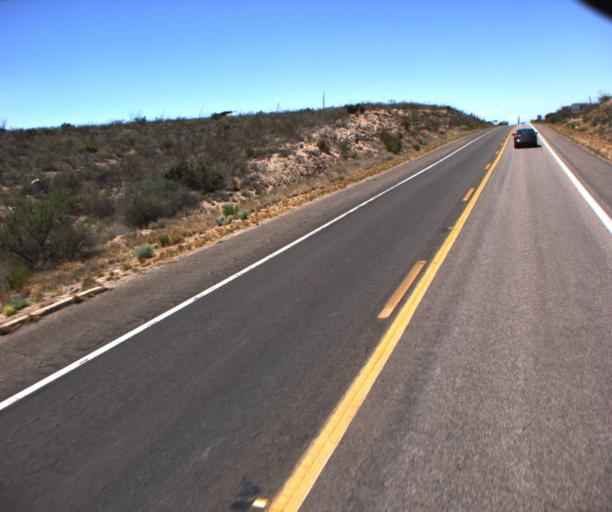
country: US
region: Arizona
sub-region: Cochise County
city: Tombstone
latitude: 31.7042
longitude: -110.0510
